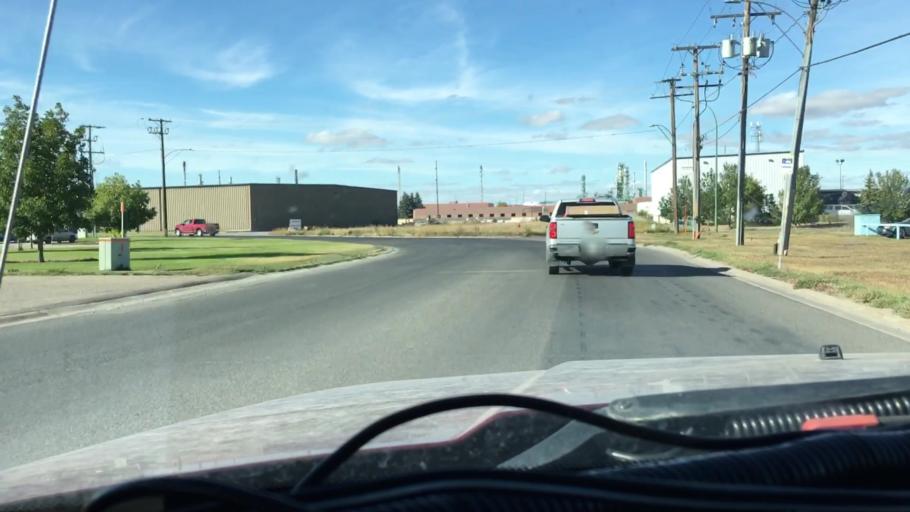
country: CA
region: Saskatchewan
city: Regina
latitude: 50.4774
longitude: -104.5616
